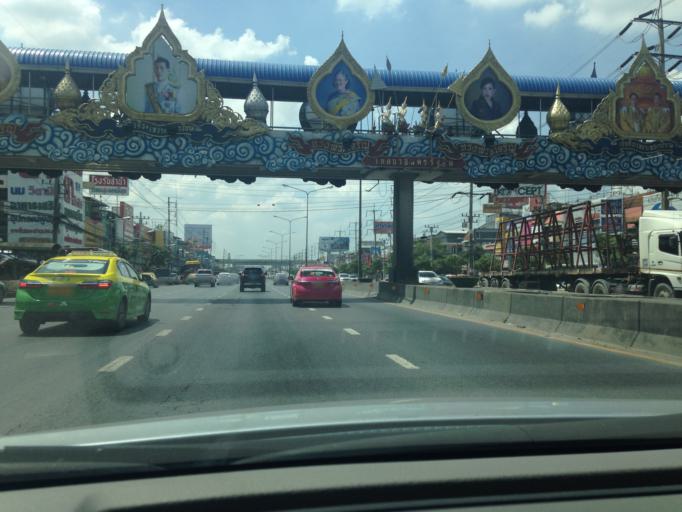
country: TH
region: Phra Nakhon Si Ayutthaya
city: Ban Bang Kadi Pathum Thani
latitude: 13.9870
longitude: 100.6081
